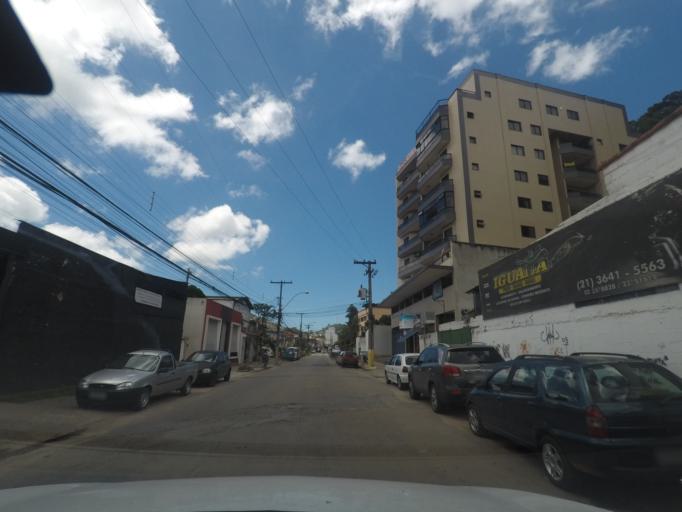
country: BR
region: Rio de Janeiro
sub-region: Teresopolis
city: Teresopolis
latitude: -22.4052
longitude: -42.9670
